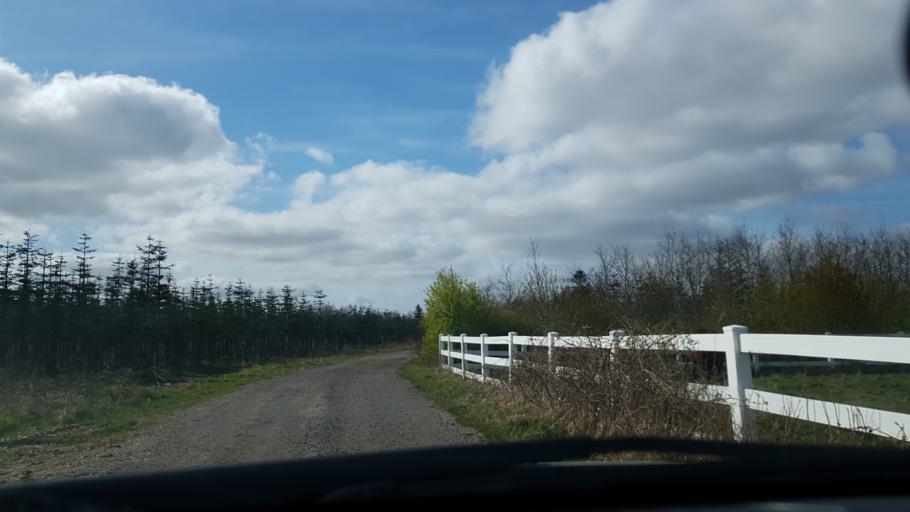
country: DK
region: South Denmark
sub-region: Haderslev Kommune
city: Gram
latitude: 55.2991
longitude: 8.9806
